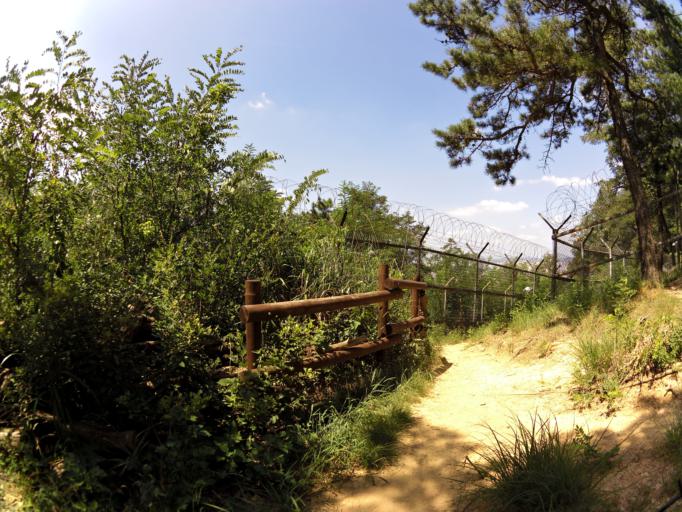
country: KR
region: Daegu
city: Daegu
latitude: 35.8602
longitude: 128.6566
